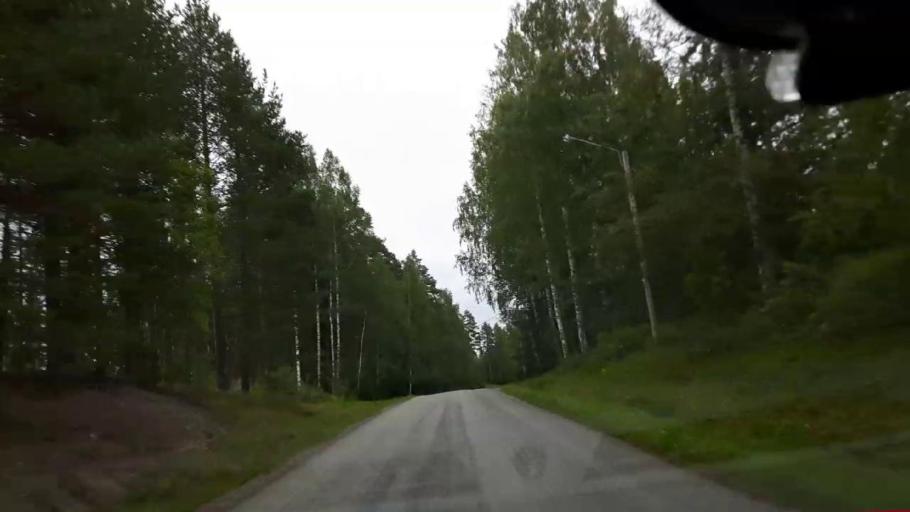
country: SE
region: Vaesternorrland
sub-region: Ange Kommun
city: Fransta
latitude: 62.7711
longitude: 16.0095
